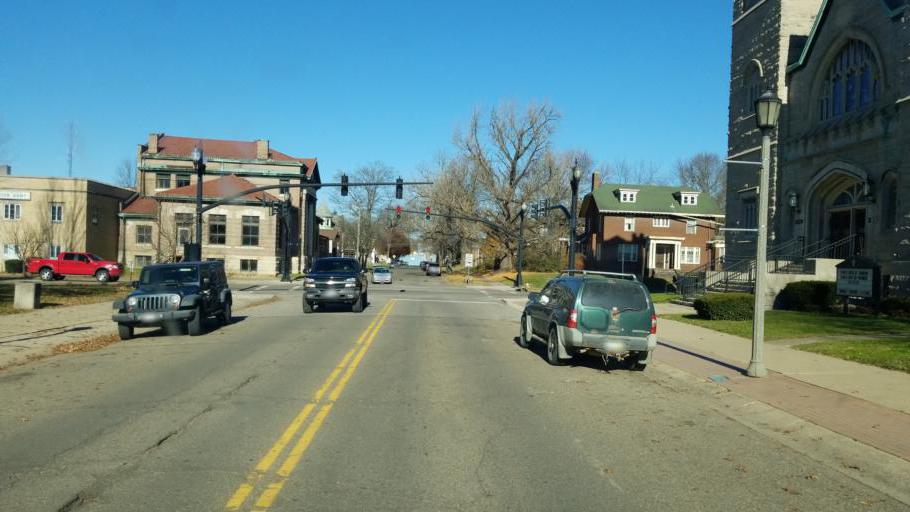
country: US
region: Ohio
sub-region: Coshocton County
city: Coshocton
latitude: 40.2745
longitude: -81.8652
